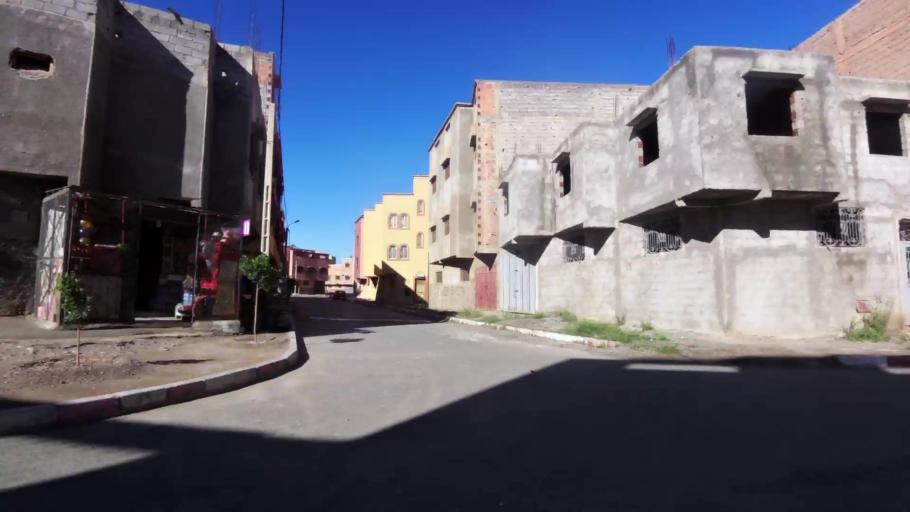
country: MA
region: Marrakech-Tensift-Al Haouz
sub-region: Marrakech
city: Marrakesh
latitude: 31.6014
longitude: -8.0356
